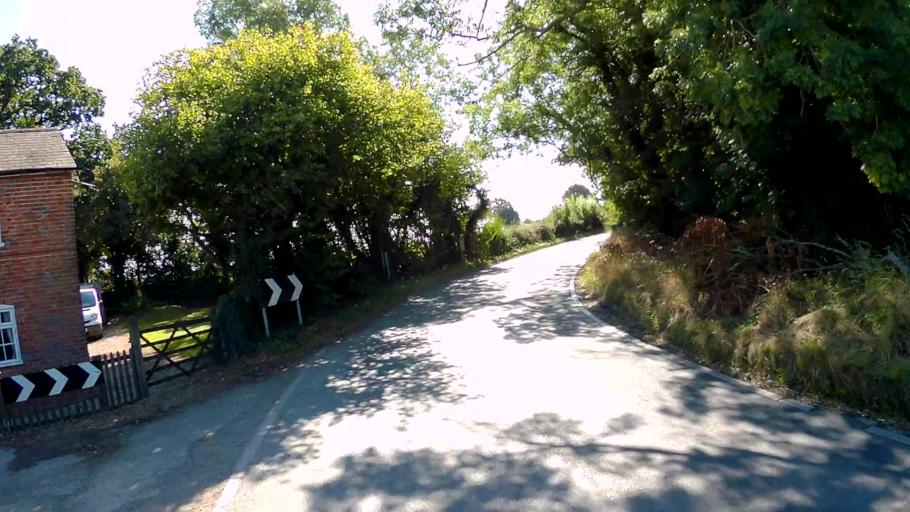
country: GB
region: England
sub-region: West Berkshire
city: Stratfield Mortimer
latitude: 51.3709
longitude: -1.0292
